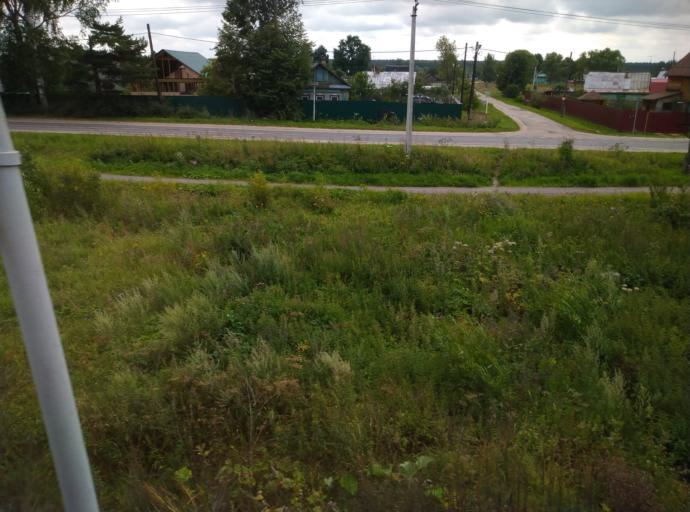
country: RU
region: Jaroslavl
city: Burmakino
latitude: 57.4370
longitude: 40.3091
